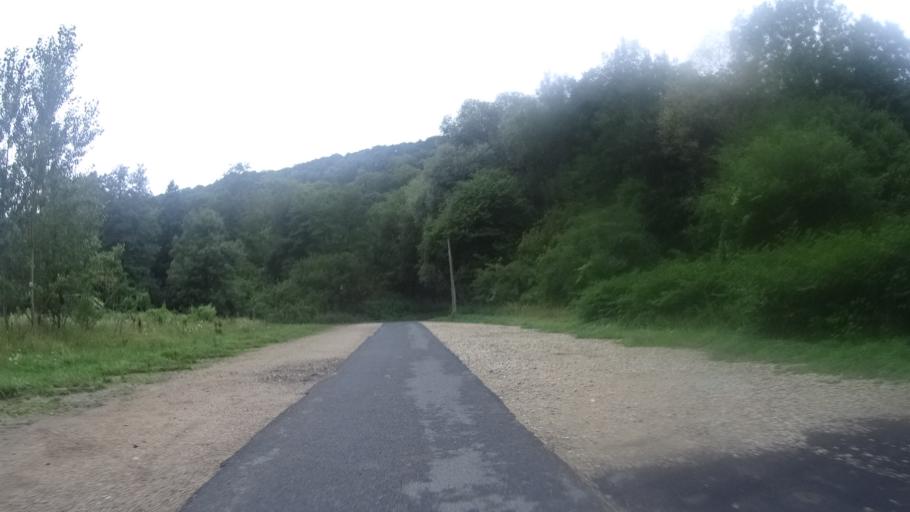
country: FR
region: Lorraine
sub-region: Departement de Meurthe-et-Moselle
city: Chaligny
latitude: 48.6353
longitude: 6.0415
